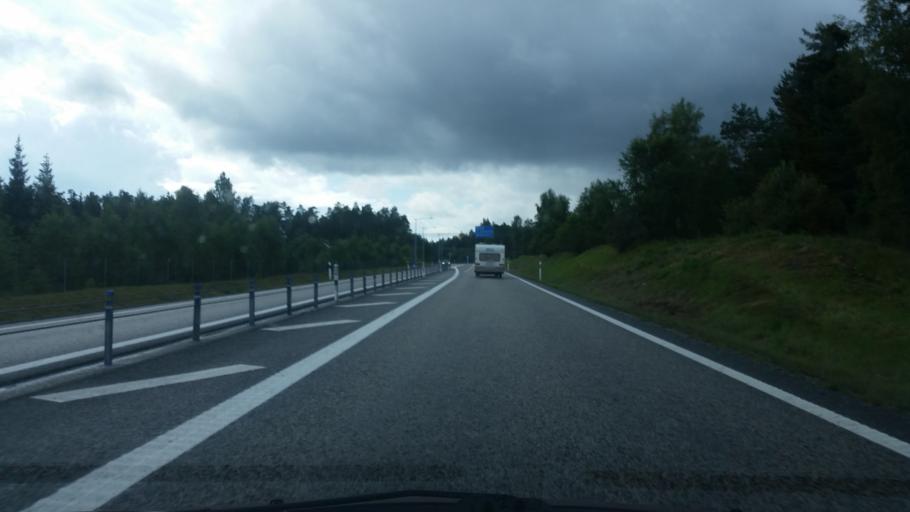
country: SE
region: Joenkoeping
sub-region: Gislaveds Kommun
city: Gislaved
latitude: 57.3435
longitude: 13.5526
